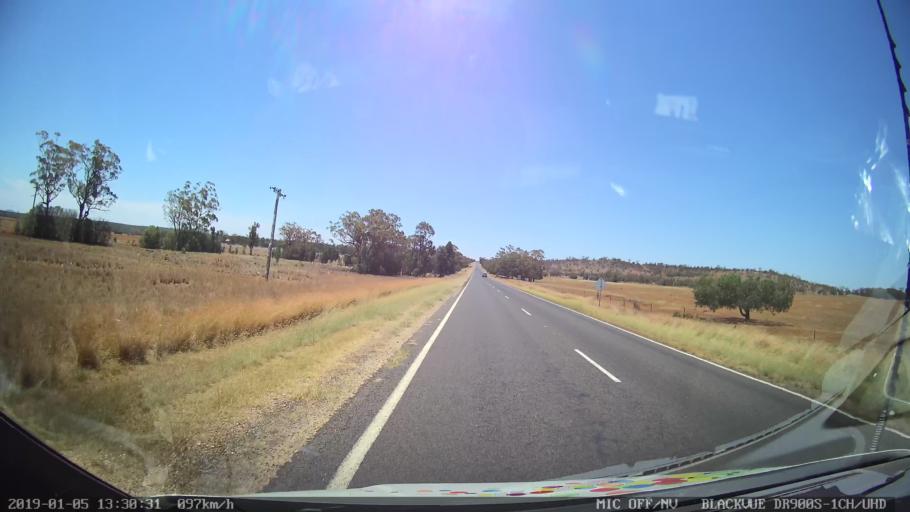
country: AU
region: New South Wales
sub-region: Gunnedah
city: Gunnedah
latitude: -31.0182
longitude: 150.0718
